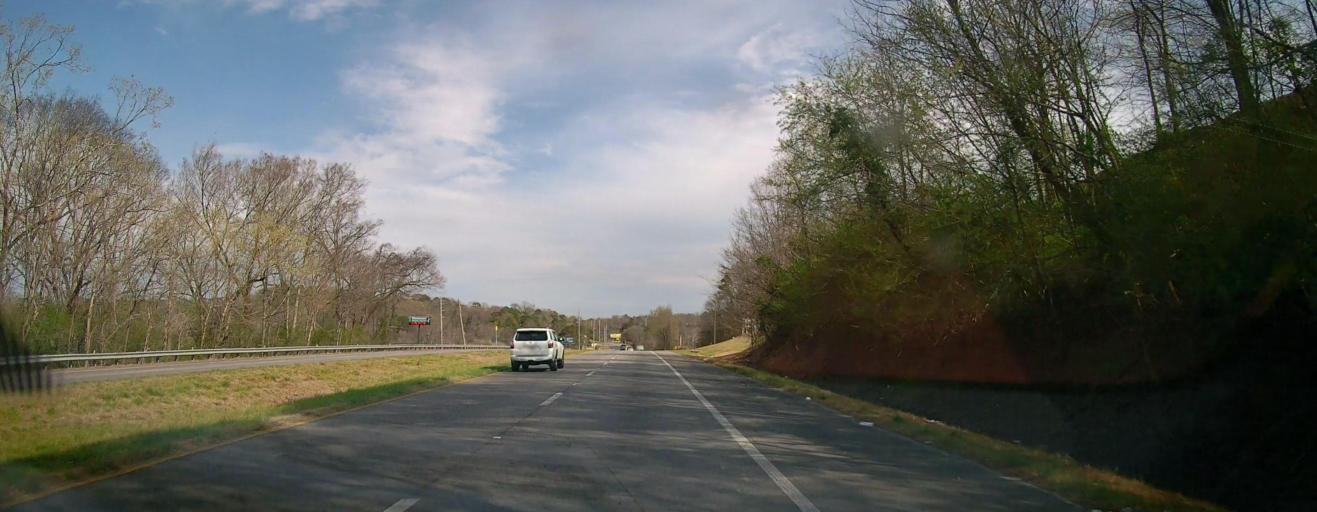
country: US
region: Alabama
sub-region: Jefferson County
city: Forestdale
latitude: 33.5795
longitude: -86.9178
